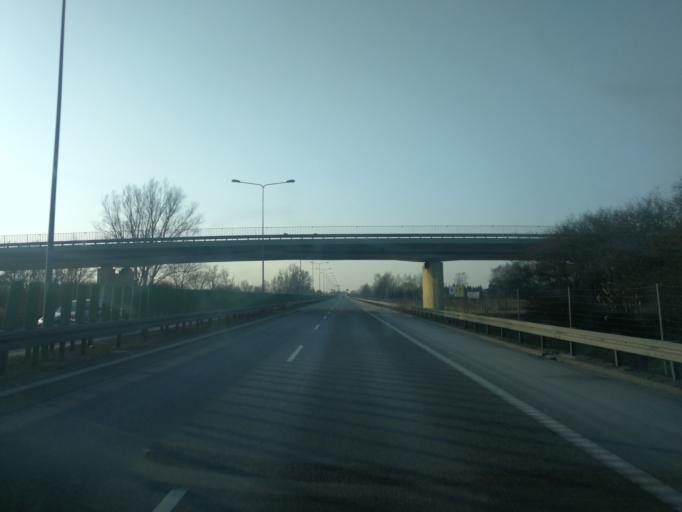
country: PL
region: Warmian-Masurian Voivodeship
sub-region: Powiat elblaski
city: Elblag
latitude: 54.1395
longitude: 19.4076
